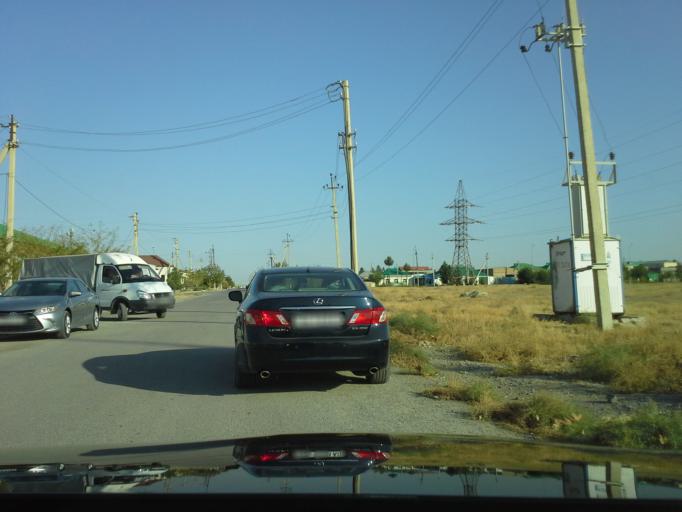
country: TM
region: Ahal
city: Abadan
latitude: 38.0496
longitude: 58.1628
